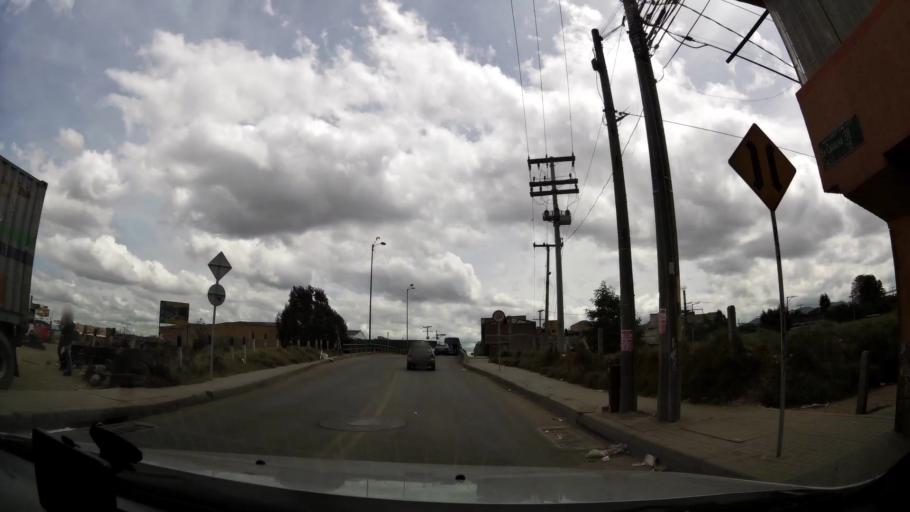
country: CO
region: Bogota D.C.
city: Bogota
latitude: 4.6530
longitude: -74.1345
